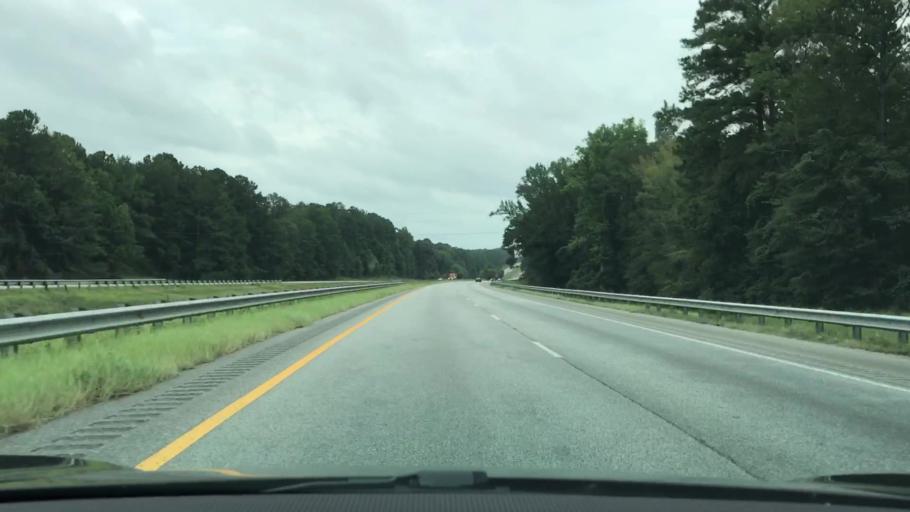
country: US
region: Alabama
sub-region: Macon County
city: Tuskegee
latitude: 32.5062
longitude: -85.6046
